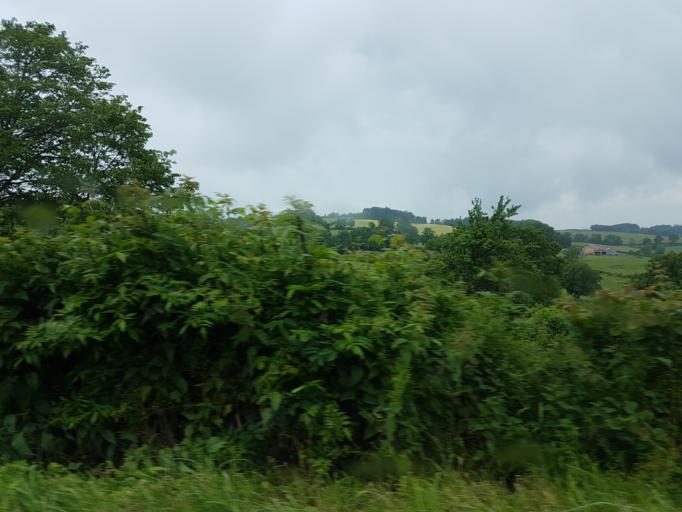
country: FR
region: Bourgogne
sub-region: Departement de la Nievre
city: Chateau-Chinon(Ville)
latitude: 47.1595
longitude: 3.8591
